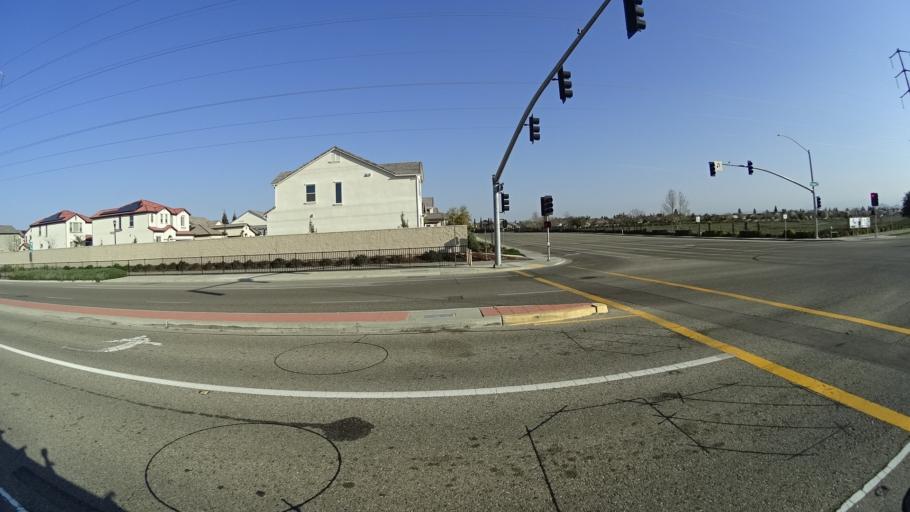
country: US
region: California
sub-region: Fresno County
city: Clovis
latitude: 36.8954
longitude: -119.7567
